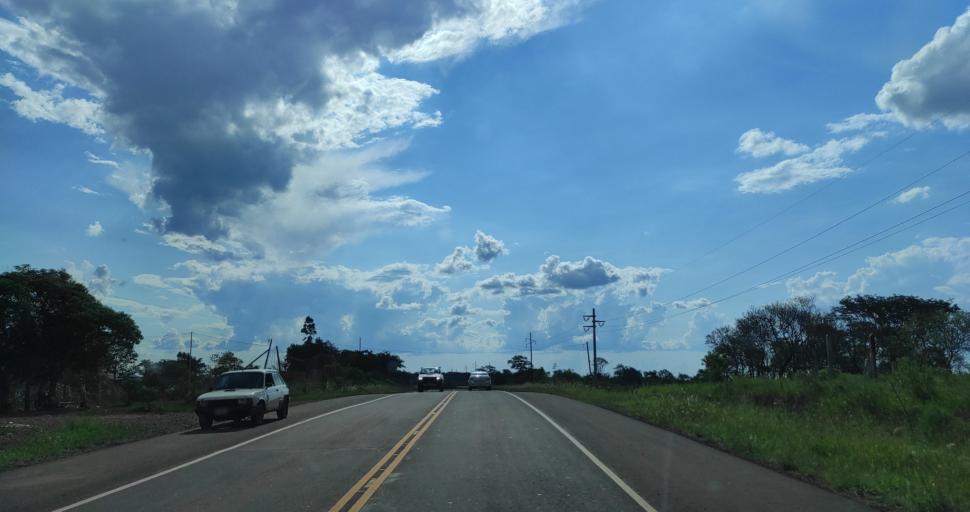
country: AR
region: Misiones
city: Bernardo de Irigoyen
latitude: -26.2985
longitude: -53.8087
